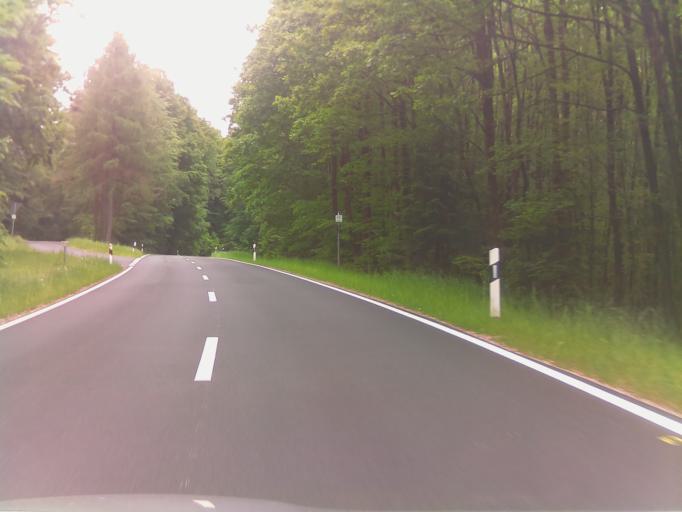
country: DE
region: Bavaria
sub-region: Regierungsbezirk Unterfranken
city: Wiesen
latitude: 50.0997
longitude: 9.3443
